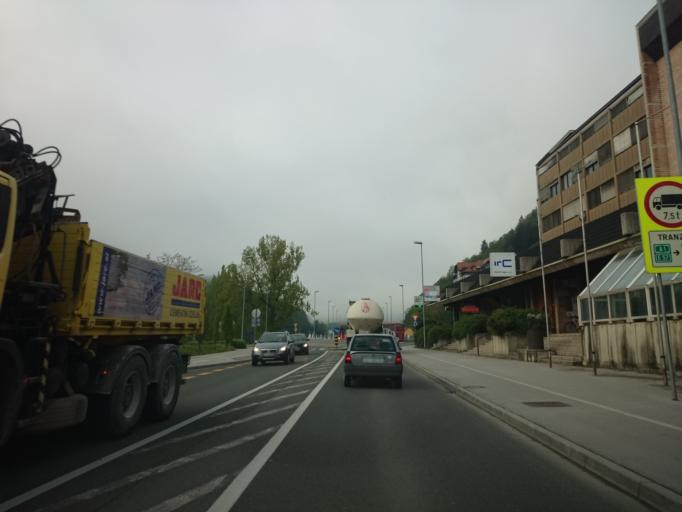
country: SI
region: Celje
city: Celje
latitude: 46.2263
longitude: 15.2667
